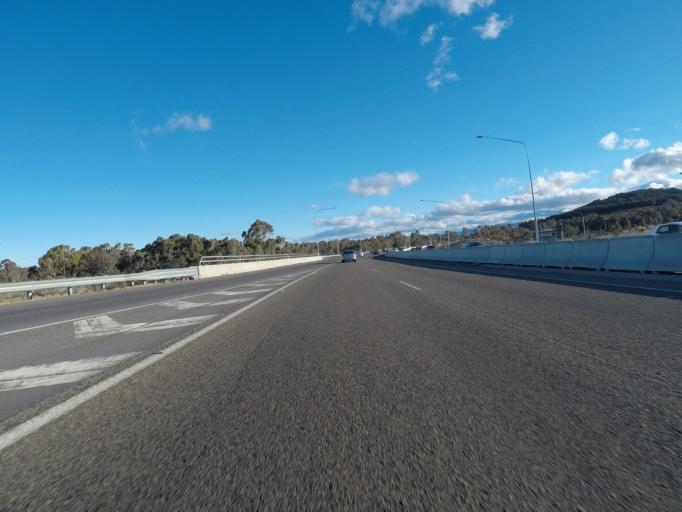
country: AU
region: Australian Capital Territory
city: Acton
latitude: -35.2836
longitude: 149.0858
